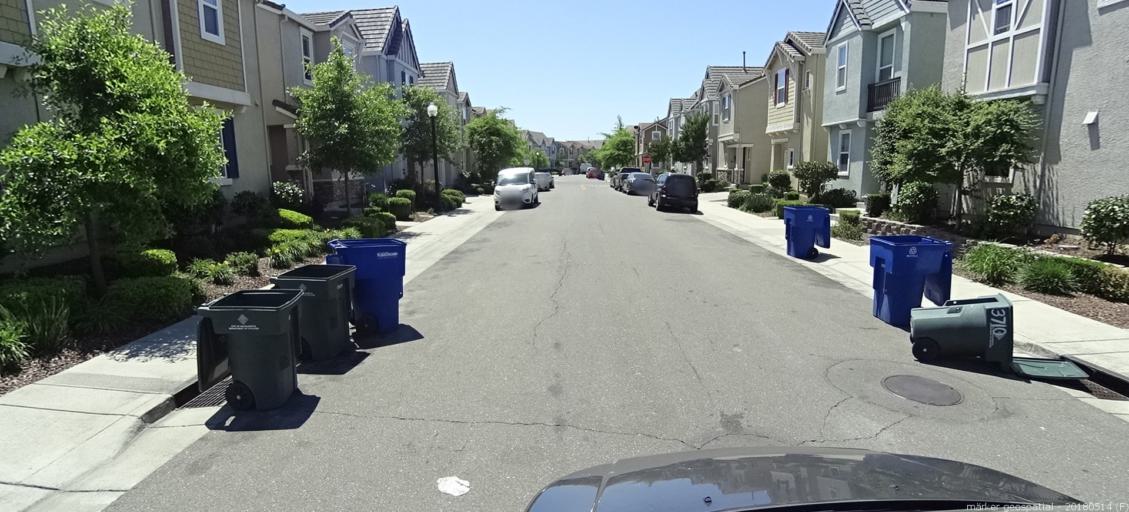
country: US
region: California
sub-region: Yolo County
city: West Sacramento
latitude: 38.6267
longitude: -121.5202
